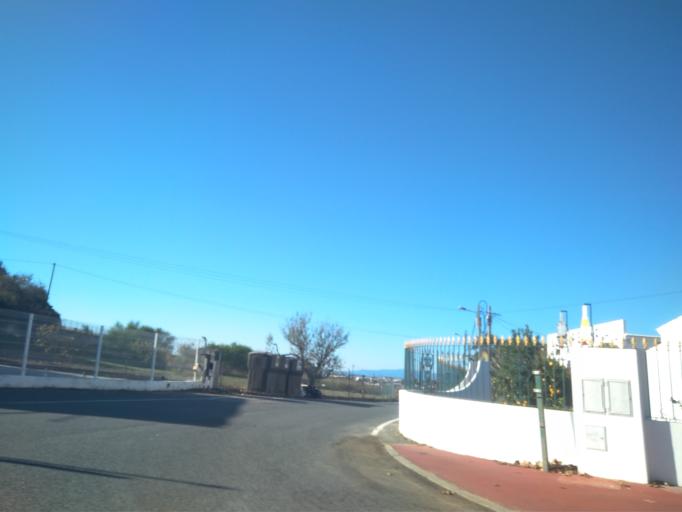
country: PT
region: Faro
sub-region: Albufeira
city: Ferreiras
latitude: 37.1176
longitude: -8.2281
